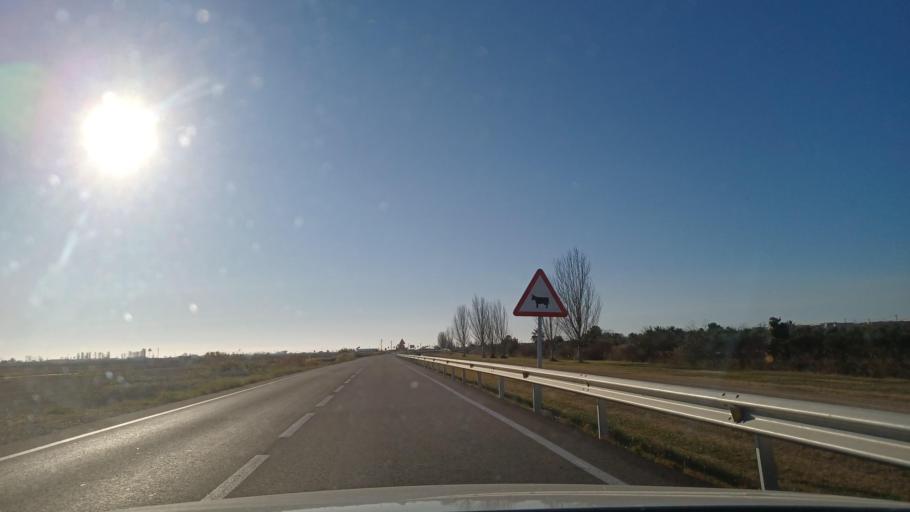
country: ES
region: Catalonia
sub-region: Provincia de Tarragona
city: Sant Carles de la Rapita
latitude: 40.6452
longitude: 0.5993
